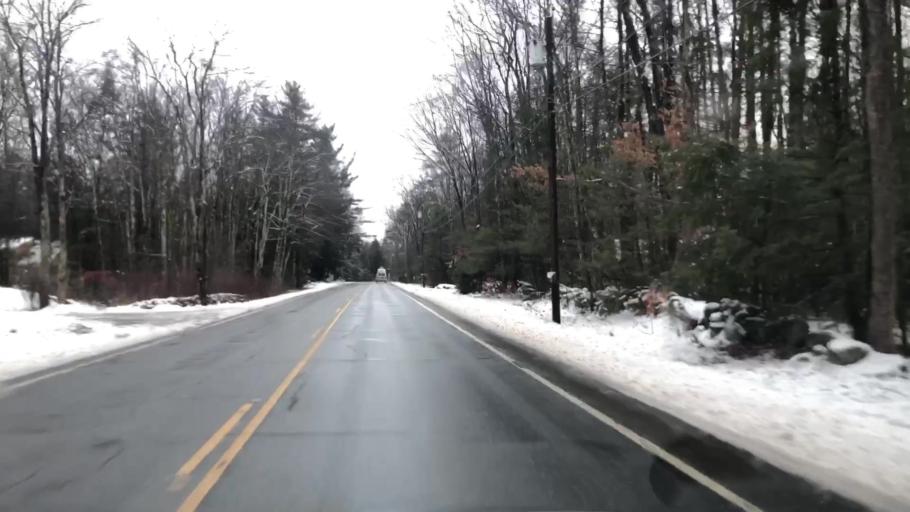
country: US
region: New Hampshire
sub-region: Hillsborough County
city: New Boston
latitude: 43.0225
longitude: -71.6918
